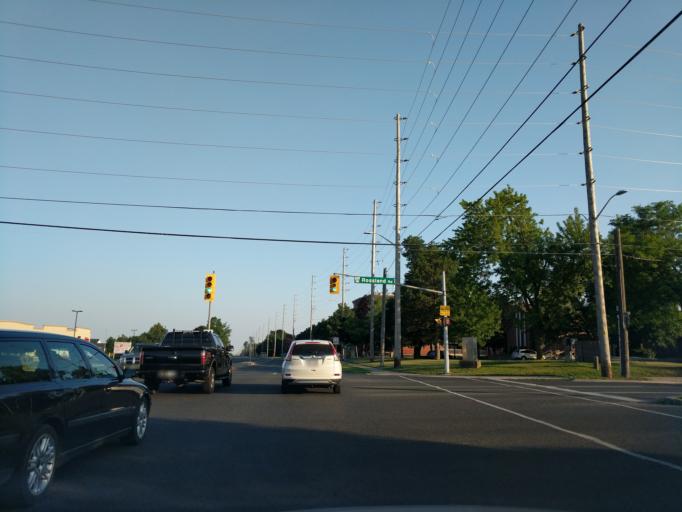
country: CA
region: Ontario
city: Oshawa
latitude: 43.9085
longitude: -78.9008
